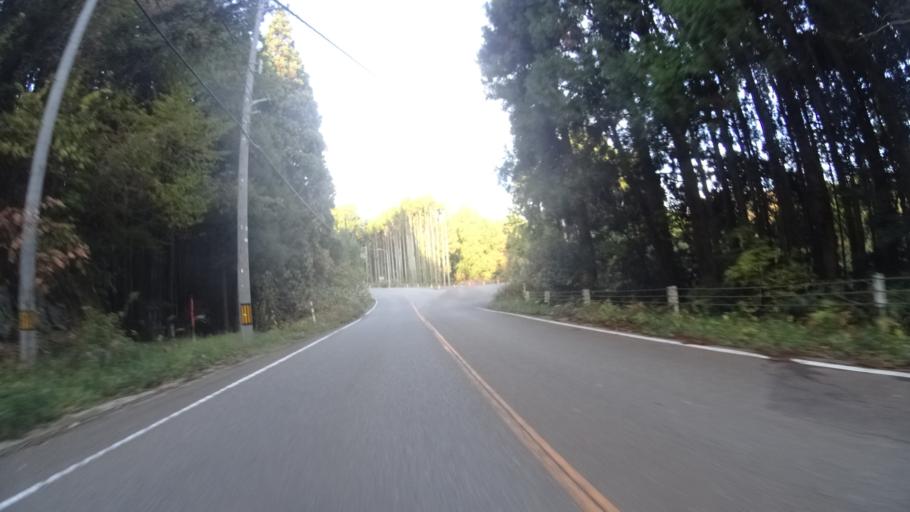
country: JP
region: Ishikawa
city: Nanao
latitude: 37.1806
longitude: 136.7136
